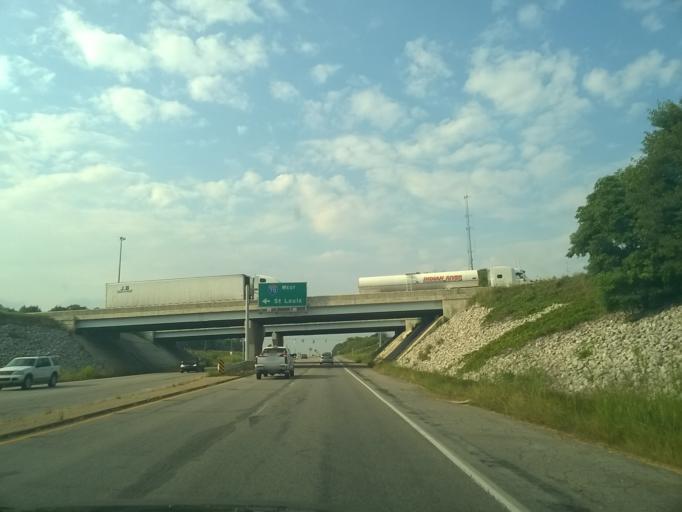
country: US
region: Indiana
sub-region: Putnam County
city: Cloverdale
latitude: 39.5326
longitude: -86.8026
